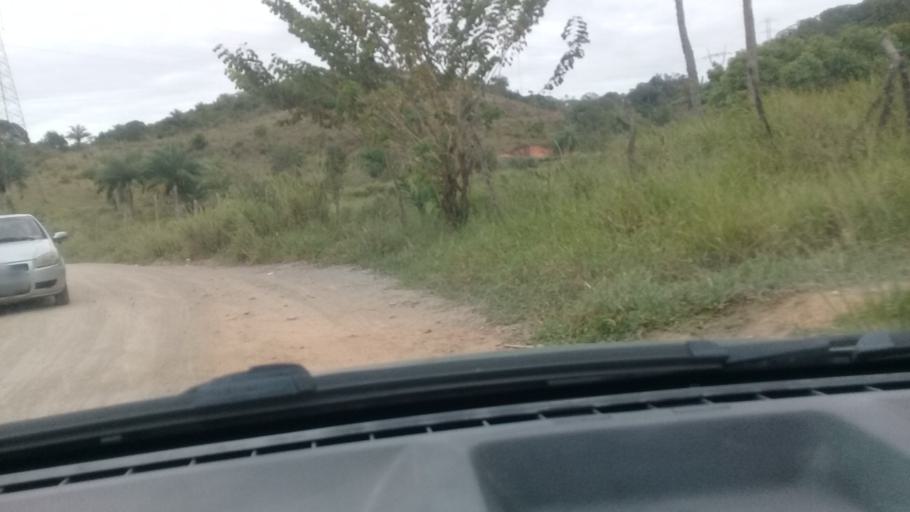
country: BR
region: Pernambuco
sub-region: Jaboatao Dos Guararapes
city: Jaboatao dos Guararapes
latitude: -8.0850
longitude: -35.0319
